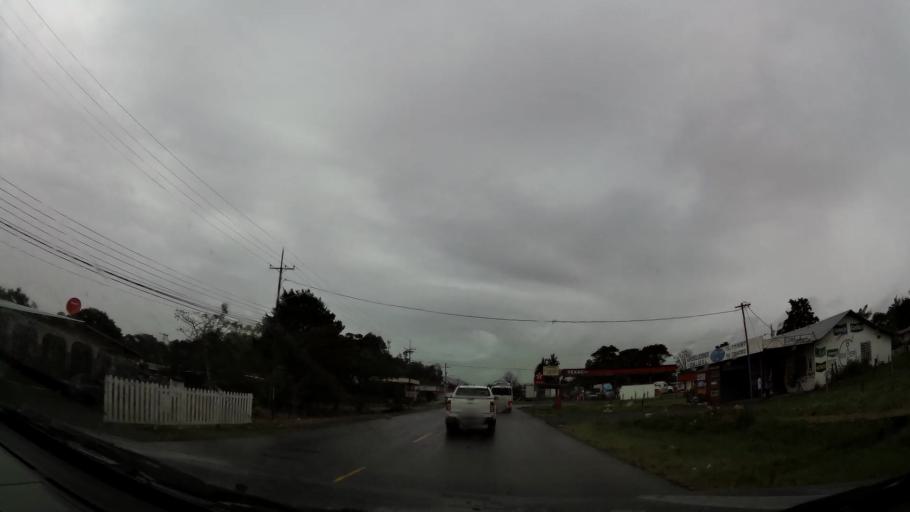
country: PA
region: Chiriqui
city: Volcan
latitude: 8.7745
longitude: -82.6376
